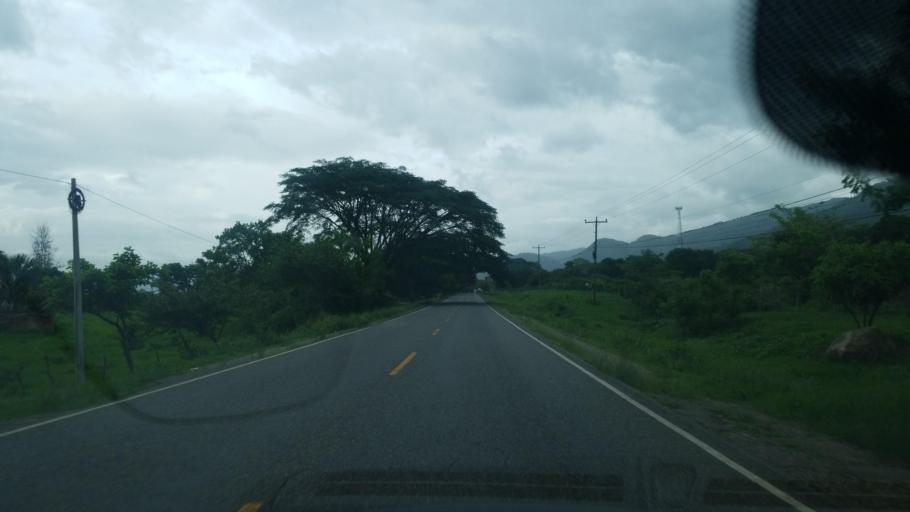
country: HN
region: Ocotepeque
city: Antigua Ocotepeque
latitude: 14.3970
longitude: -89.1994
